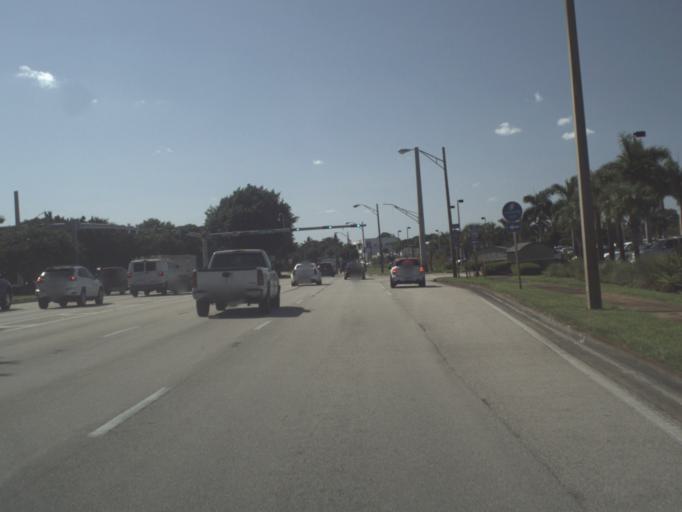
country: US
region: Florida
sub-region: Collier County
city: Naples
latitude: 26.1727
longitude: -81.7999
